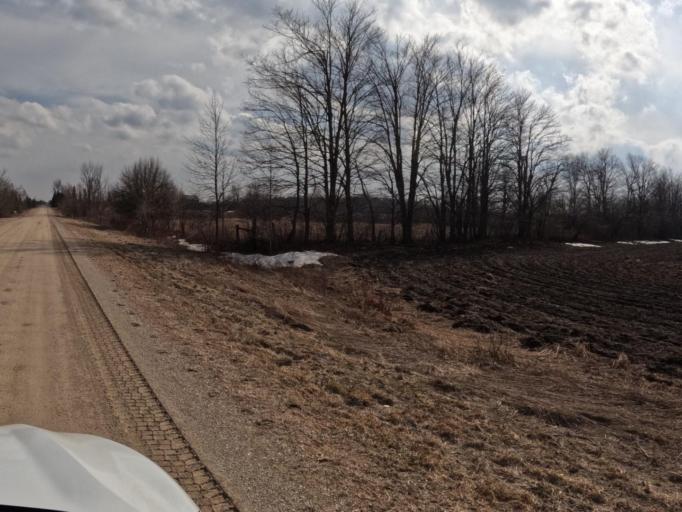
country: CA
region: Ontario
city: Shelburne
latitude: 43.9386
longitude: -80.3103
